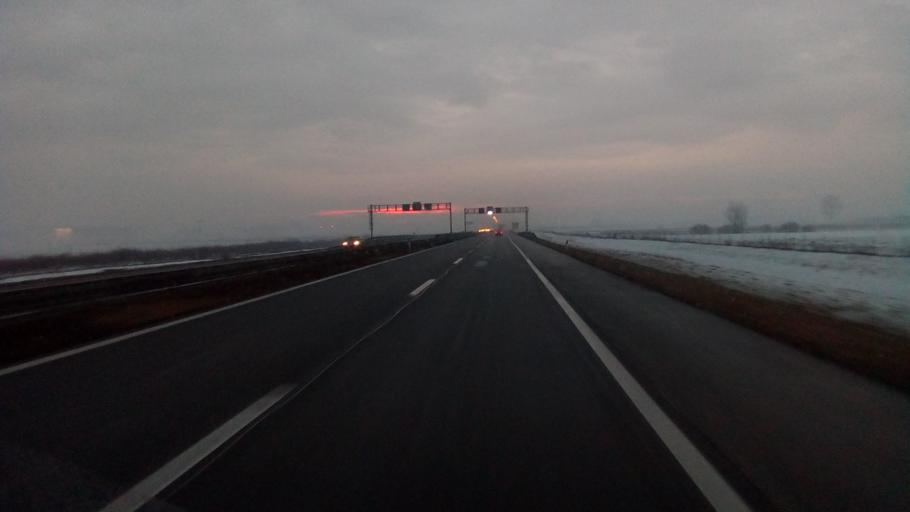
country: HR
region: Zagrebacka
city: Brckovljani
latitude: 45.7714
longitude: 16.2109
